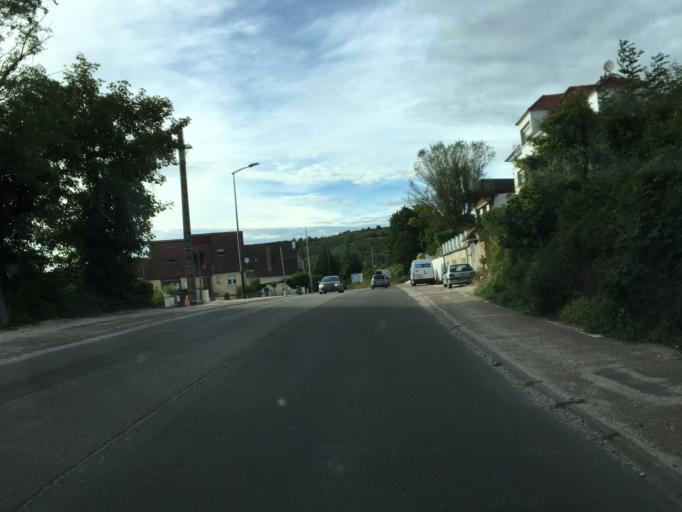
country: FR
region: Bourgogne
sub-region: Departement de la Cote-d'Or
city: Talant
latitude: 47.3326
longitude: 4.9891
